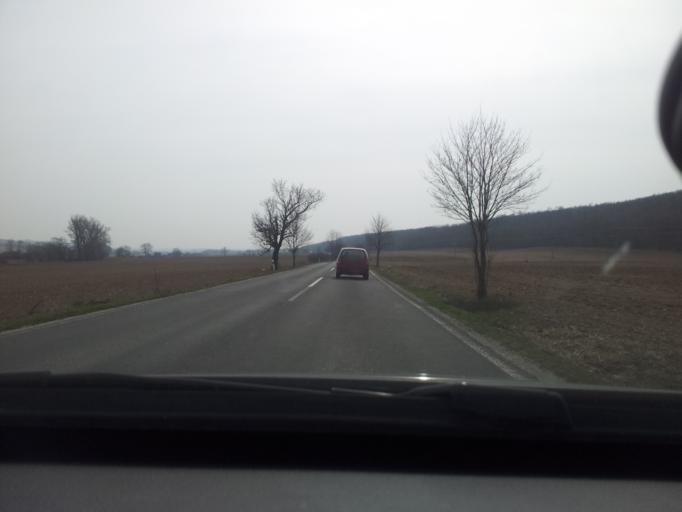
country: SK
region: Trnavsky
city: Hlohovec
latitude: 48.4045
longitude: 17.8438
